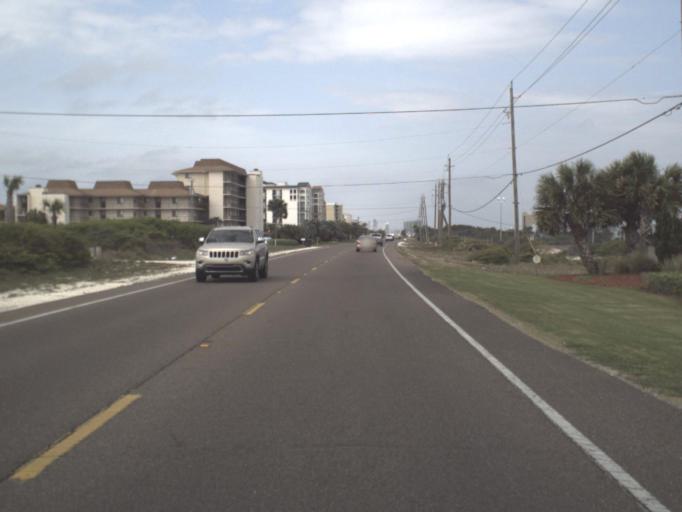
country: US
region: Alabama
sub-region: Baldwin County
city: Orange Beach
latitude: 30.2864
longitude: -87.4926
